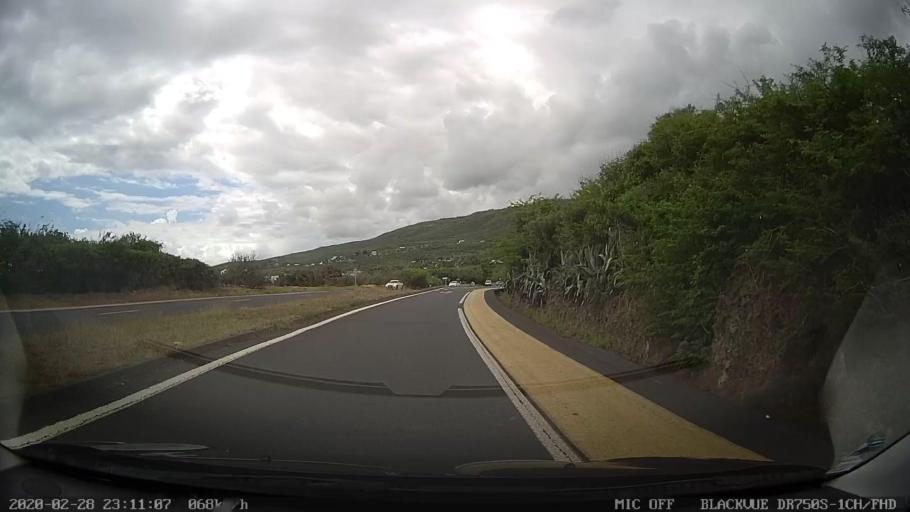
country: RE
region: Reunion
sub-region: Reunion
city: Trois-Bassins
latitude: -21.1123
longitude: 55.2557
